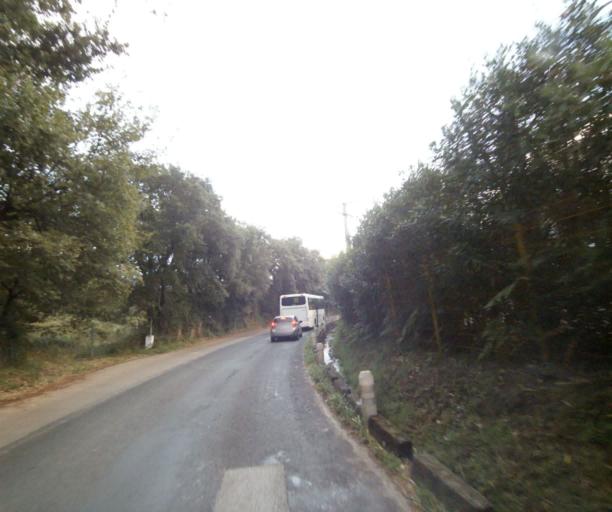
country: FR
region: Languedoc-Roussillon
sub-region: Departement des Pyrenees-Orientales
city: Argelers
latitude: 42.5611
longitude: 3.0194
